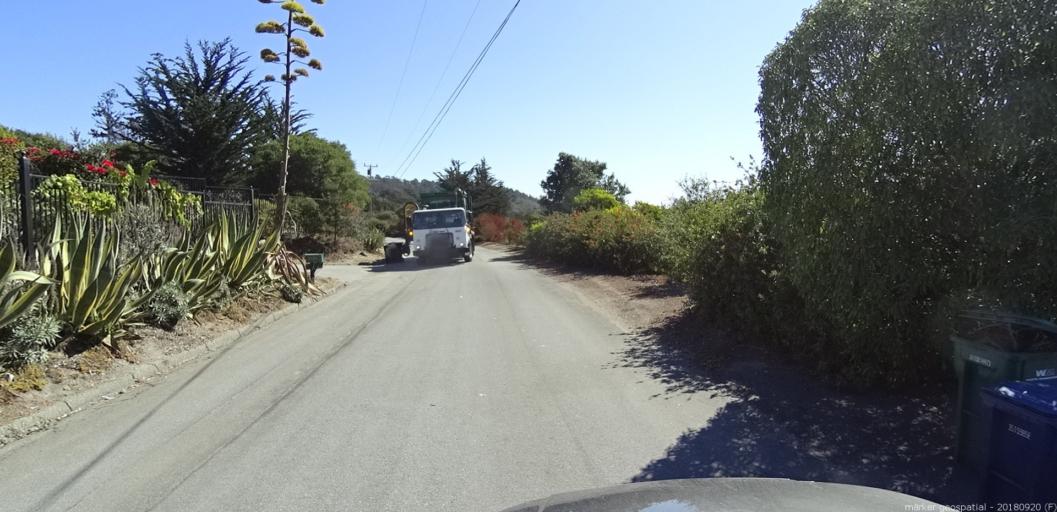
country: US
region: California
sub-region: Monterey County
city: Carmel-by-the-Sea
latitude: 36.5458
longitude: -121.9011
